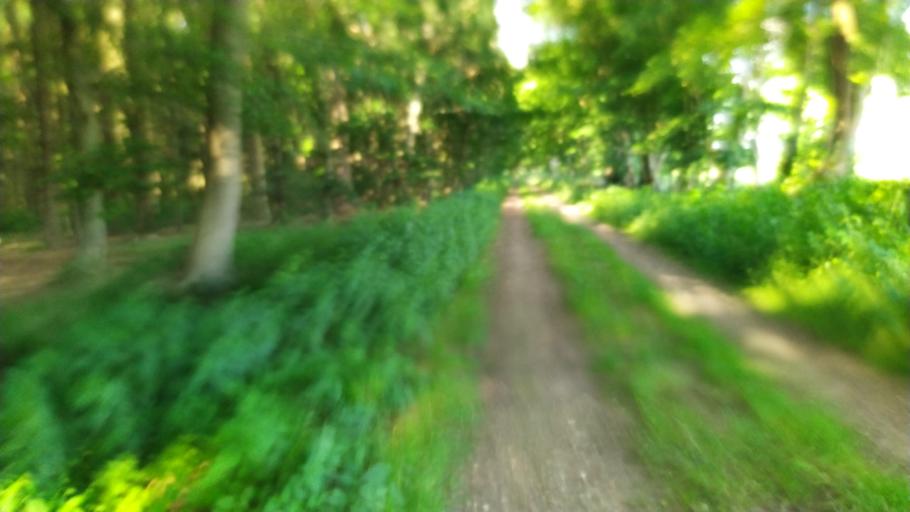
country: DE
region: Lower Saxony
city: Lintig
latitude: 53.5949
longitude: 8.9064
